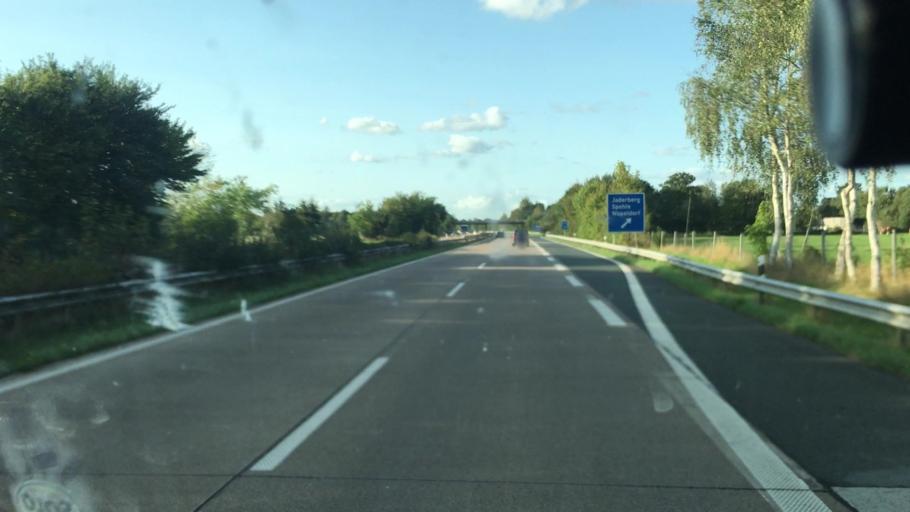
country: DE
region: Lower Saxony
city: Varel
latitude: 53.3238
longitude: 8.1383
